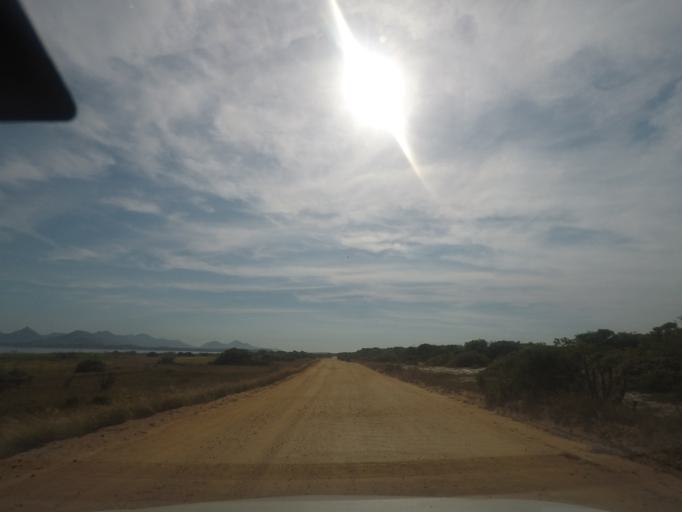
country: BR
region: Rio de Janeiro
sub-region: Marica
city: Marica
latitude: -22.9599
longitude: -42.8692
